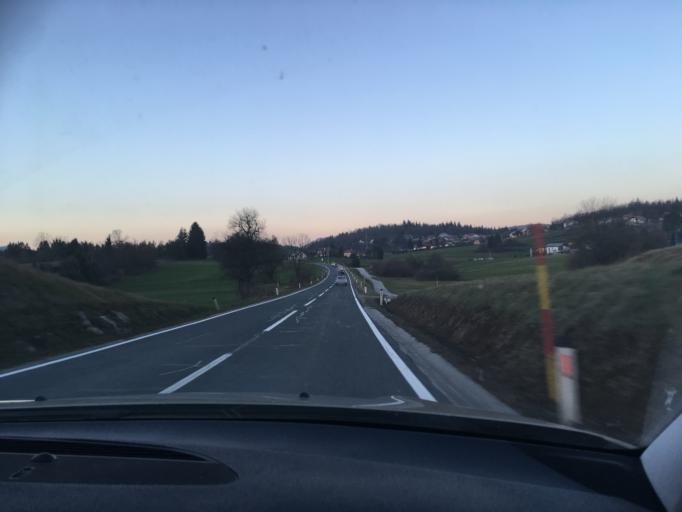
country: SI
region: Velike Lasce
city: Velike Lasce
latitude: 45.8378
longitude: 14.6342
